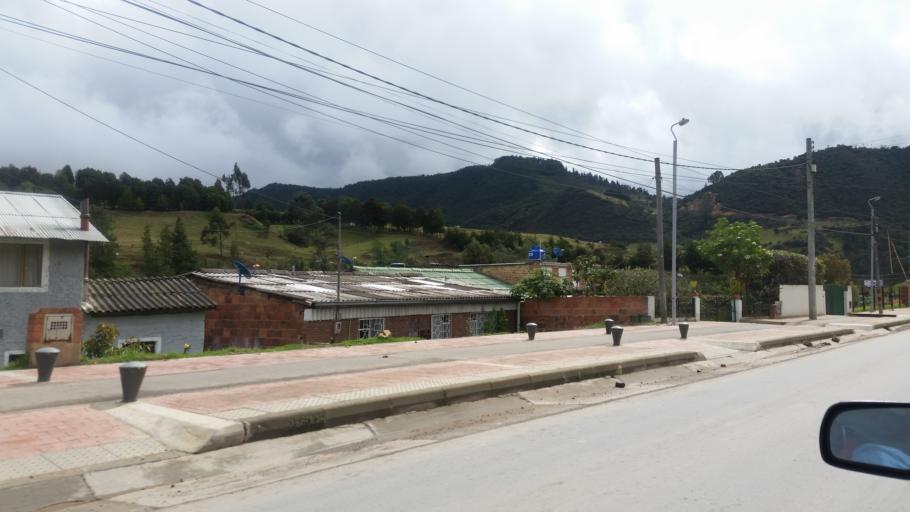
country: CO
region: Cundinamarca
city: La Calera
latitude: 4.7237
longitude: -73.9572
